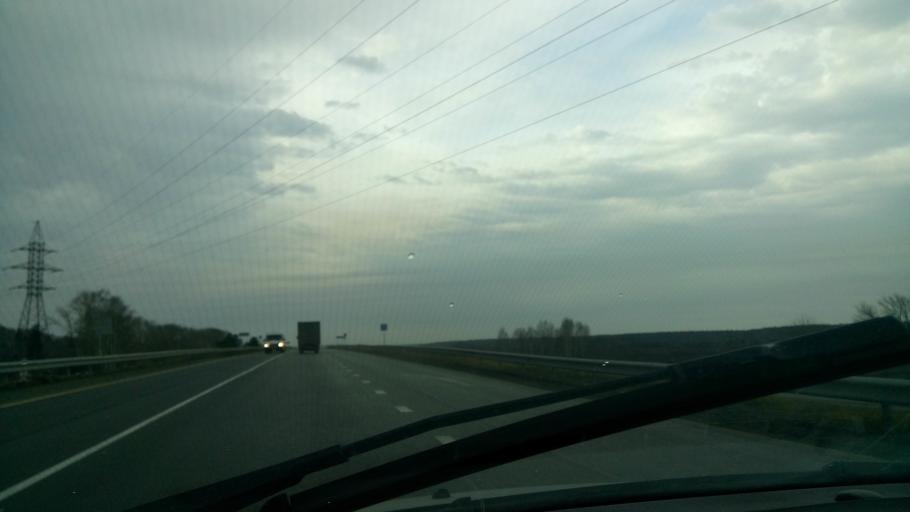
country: RU
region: Sverdlovsk
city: Obukhovskoye
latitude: 56.8421
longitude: 62.5871
